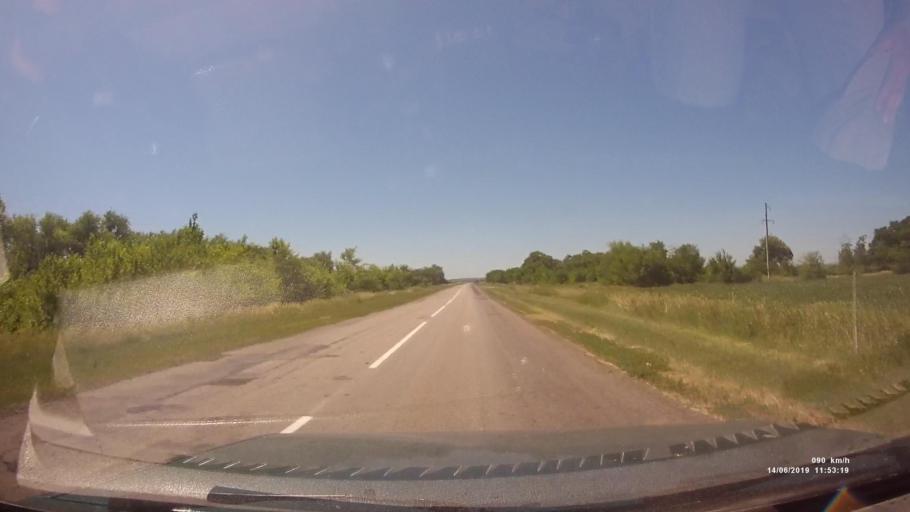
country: RU
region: Rostov
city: Kazanskaya
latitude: 49.8284
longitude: 41.2139
